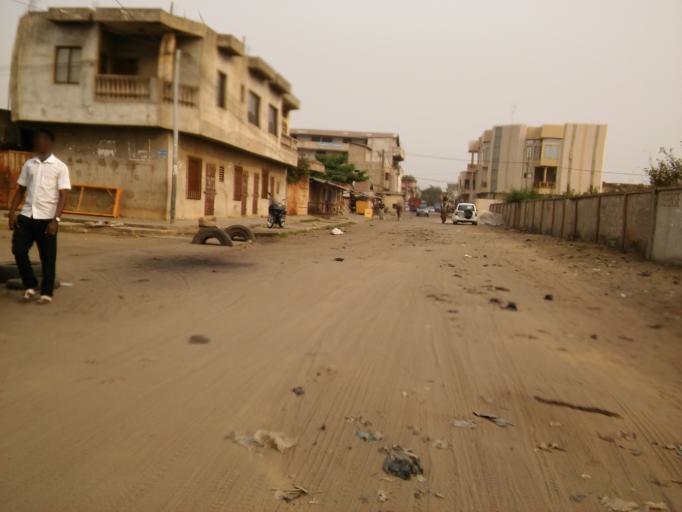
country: BJ
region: Littoral
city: Cotonou
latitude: 6.3747
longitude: 2.4096
